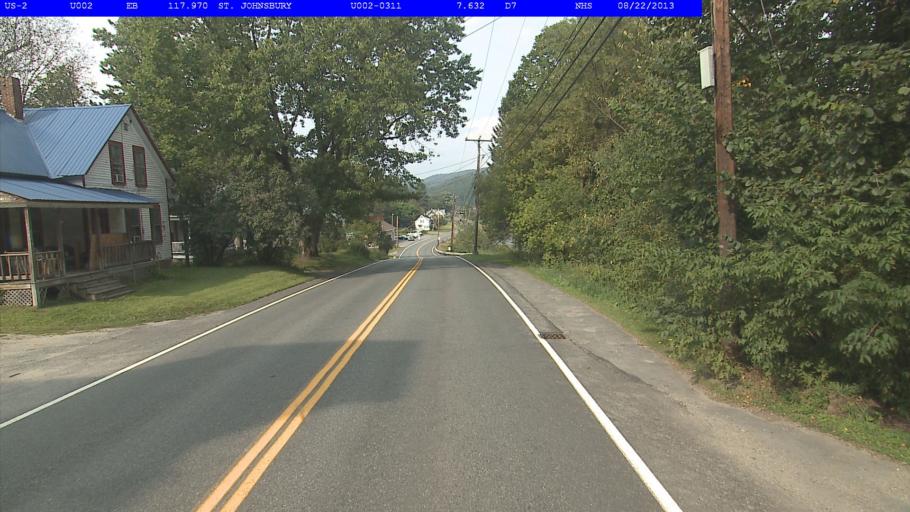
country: US
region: Vermont
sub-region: Caledonia County
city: St Johnsbury
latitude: 44.4382
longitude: -71.9469
